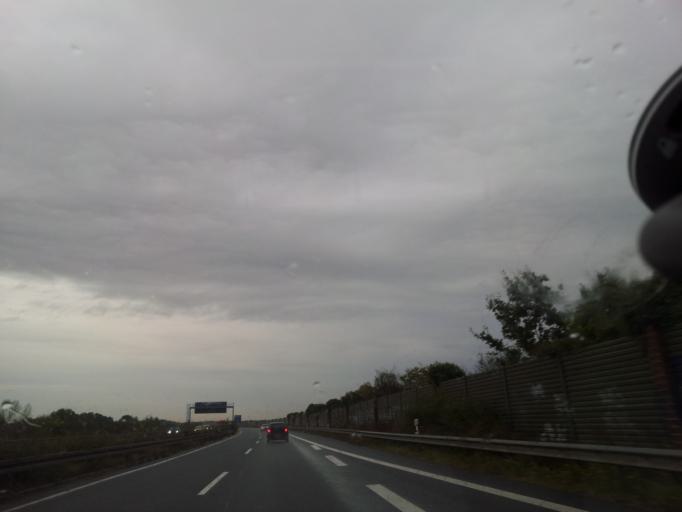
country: DE
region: Lower Saxony
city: Vordorf
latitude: 52.3215
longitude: 10.5240
